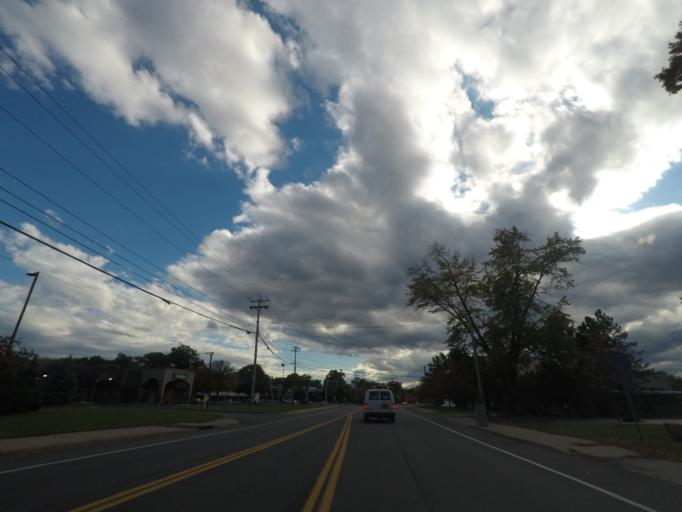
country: US
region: New York
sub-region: Albany County
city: Colonie
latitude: 42.7447
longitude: -73.8387
